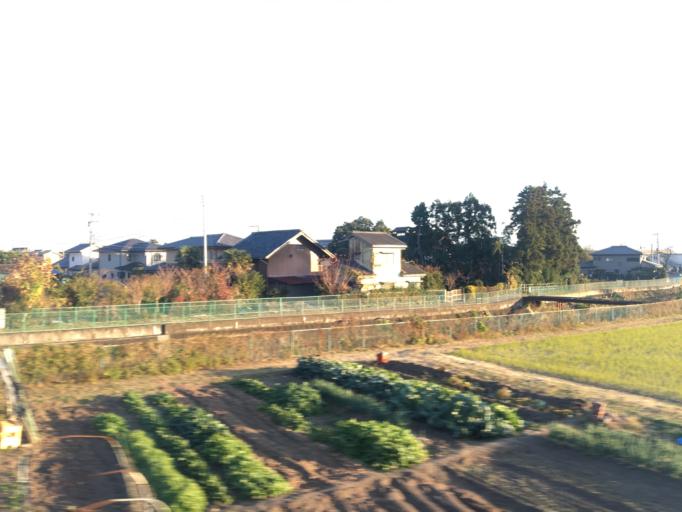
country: JP
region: Gunma
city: Maebashi-shi
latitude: 36.3732
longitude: 139.0393
